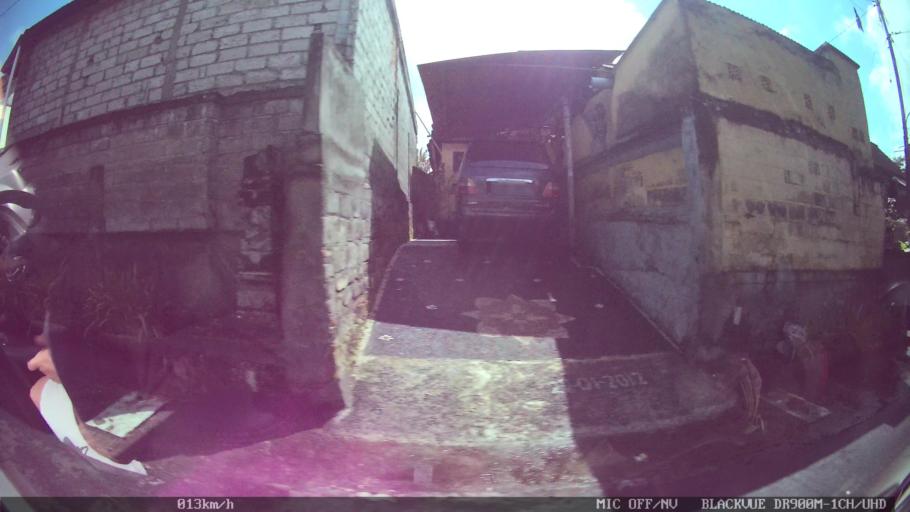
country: ID
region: Bali
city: Banjar Tebongkang
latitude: -8.5461
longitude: 115.2753
